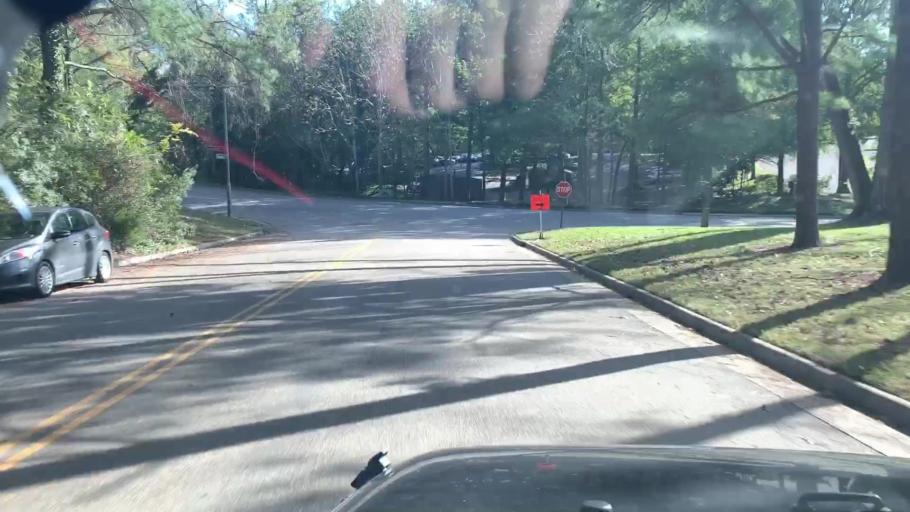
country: US
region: Virginia
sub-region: City of Williamsburg
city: Williamsburg
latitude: 37.2672
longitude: -76.7037
